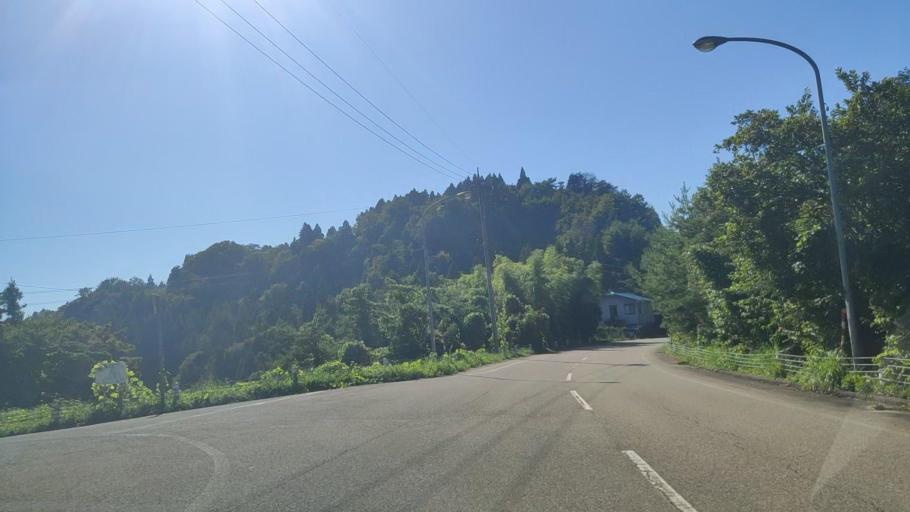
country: JP
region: Ishikawa
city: Nanao
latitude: 37.3146
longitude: 137.1561
